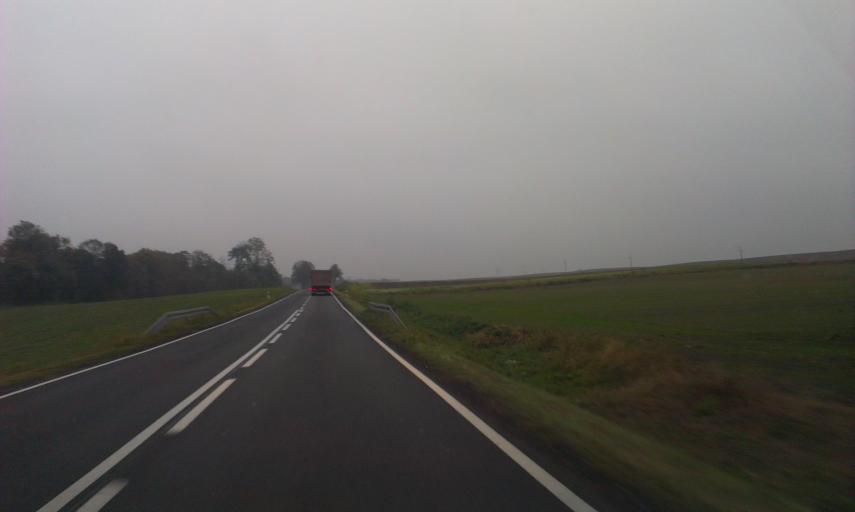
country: PL
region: Kujawsko-Pomorskie
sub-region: Powiat sepolenski
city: Sosno
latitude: 53.4417
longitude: 17.6708
